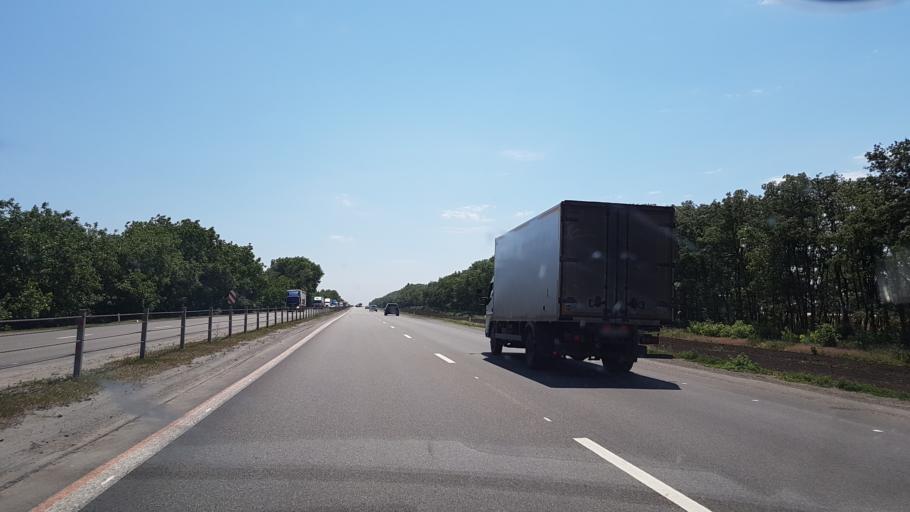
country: RU
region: Rostov
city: Grushevskaya
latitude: 47.5632
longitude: 39.9676
